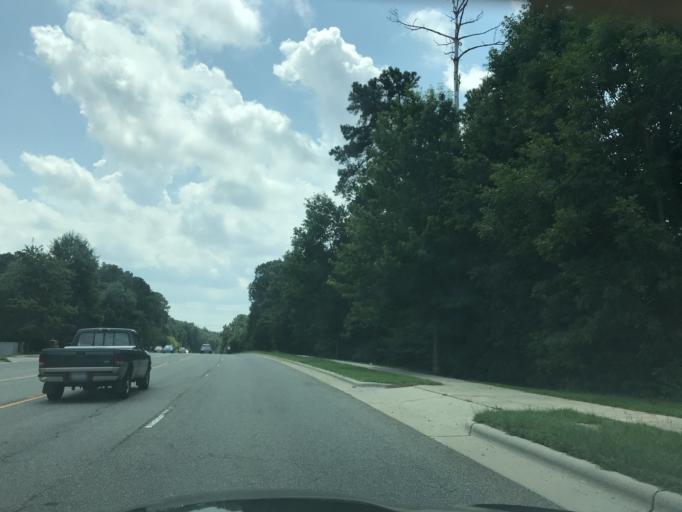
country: US
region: North Carolina
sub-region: Wake County
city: West Raleigh
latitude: 35.8514
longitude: -78.7113
